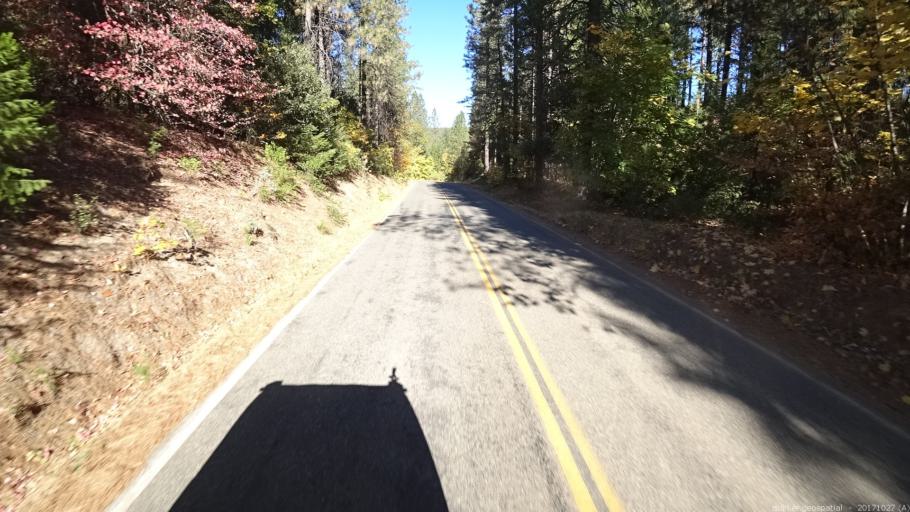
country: US
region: California
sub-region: Shasta County
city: Shingletown
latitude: 40.6968
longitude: -121.9257
